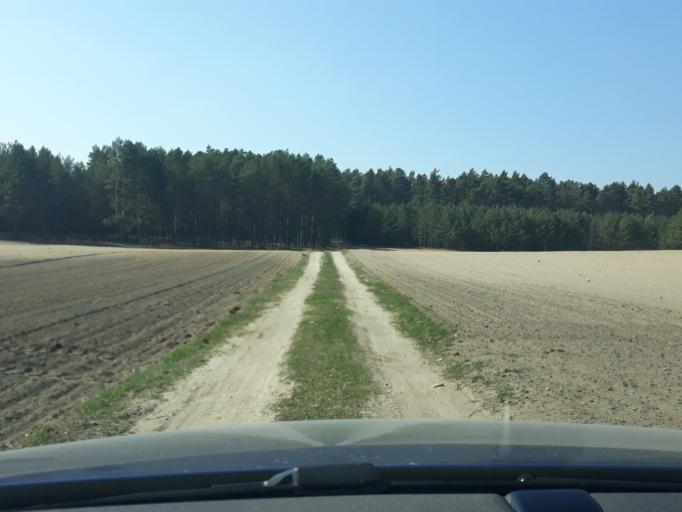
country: PL
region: Pomeranian Voivodeship
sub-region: Powiat bytowski
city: Lipnica
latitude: 53.8608
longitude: 17.4324
